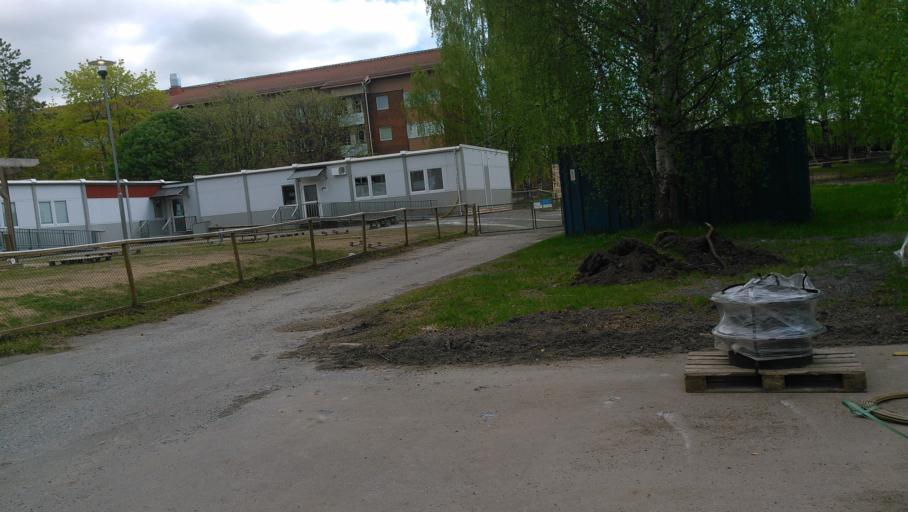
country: SE
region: Vaesterbotten
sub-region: Umea Kommun
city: Umea
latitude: 63.8123
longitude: 20.3115
